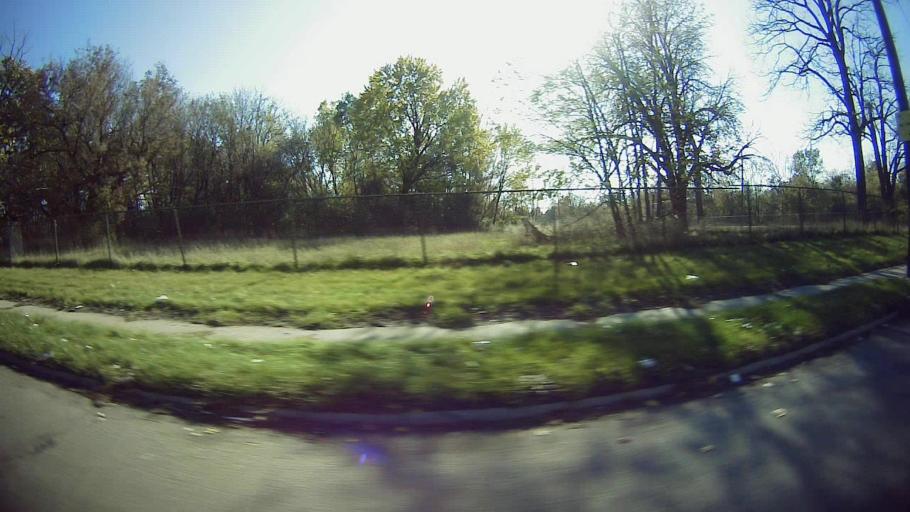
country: US
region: Michigan
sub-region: Wayne County
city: Redford
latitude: 42.4290
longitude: -83.2673
